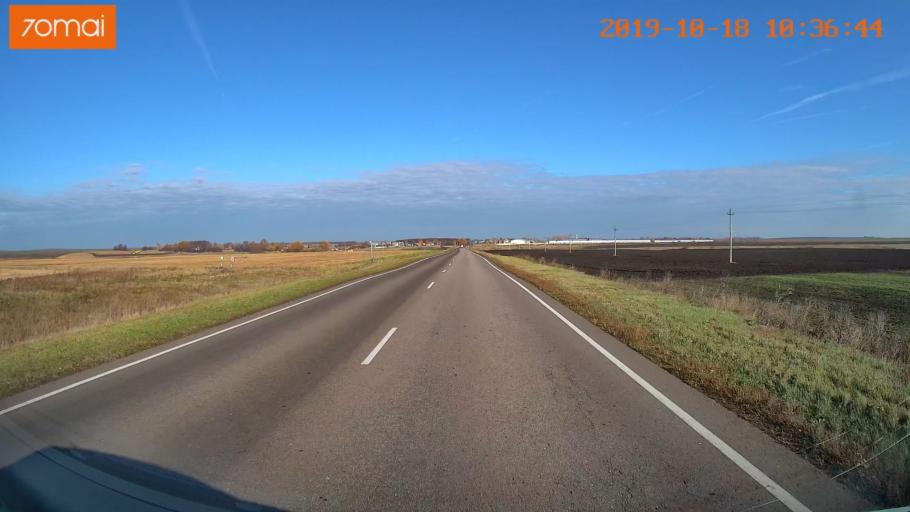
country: RU
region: Tula
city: Kurkino
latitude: 53.5525
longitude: 38.6274
